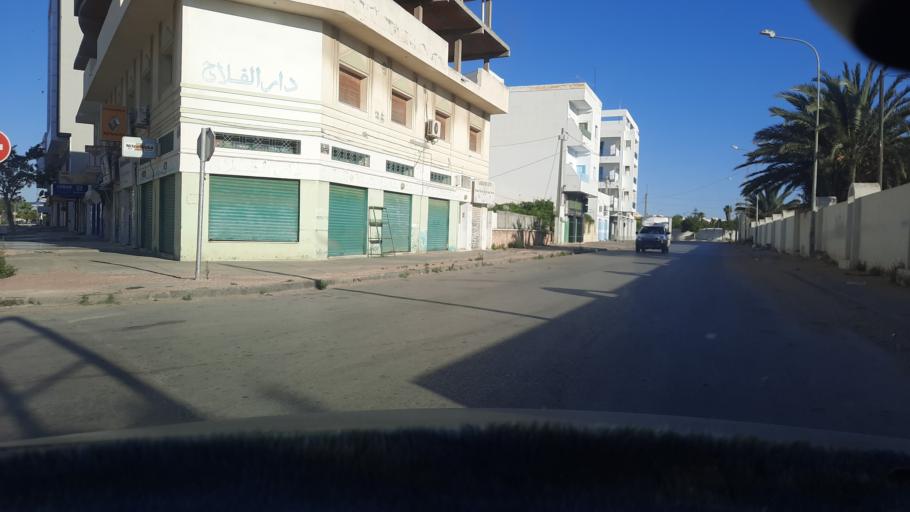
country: TN
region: Safaqis
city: Sfax
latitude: 34.7320
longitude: 10.7512
